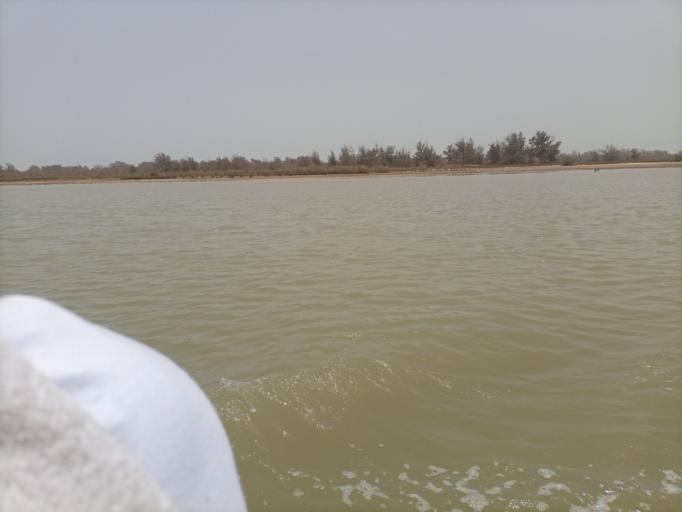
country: SN
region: Saint-Louis
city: Saint-Louis
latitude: 15.8514
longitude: -16.5177
